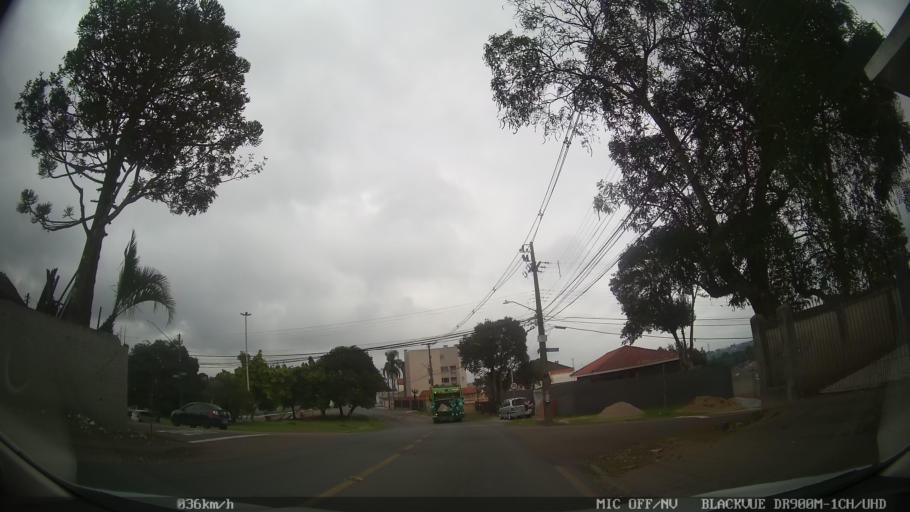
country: BR
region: Parana
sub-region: Almirante Tamandare
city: Almirante Tamandare
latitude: -25.3663
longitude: -49.2725
